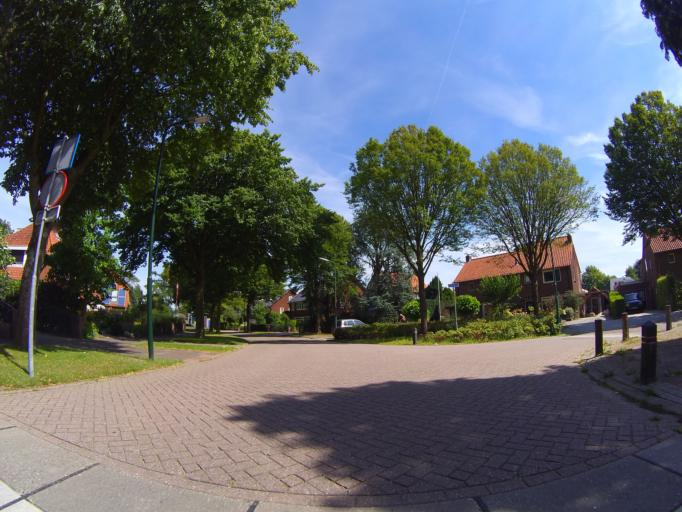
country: NL
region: Utrecht
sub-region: Gemeente Soest
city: Soest
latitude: 52.1621
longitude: 5.3069
